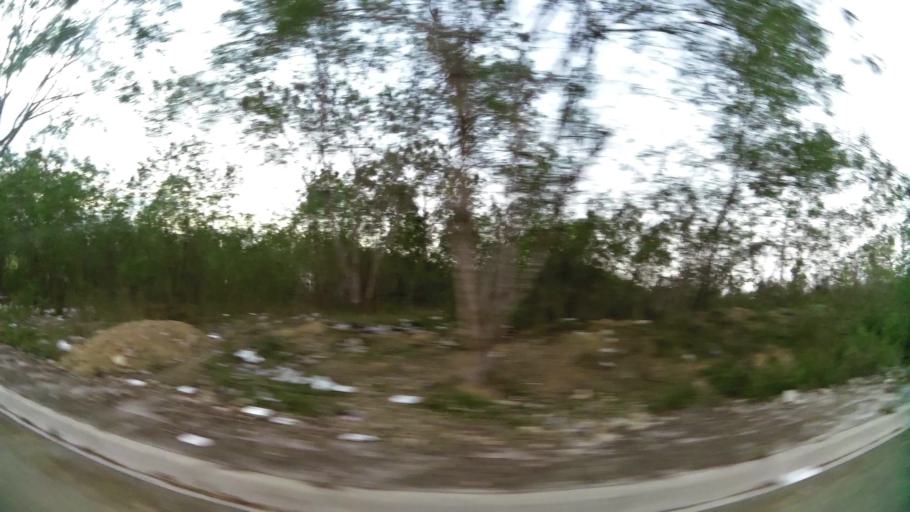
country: DO
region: Nacional
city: La Agustina
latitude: 18.5427
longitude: -69.9481
